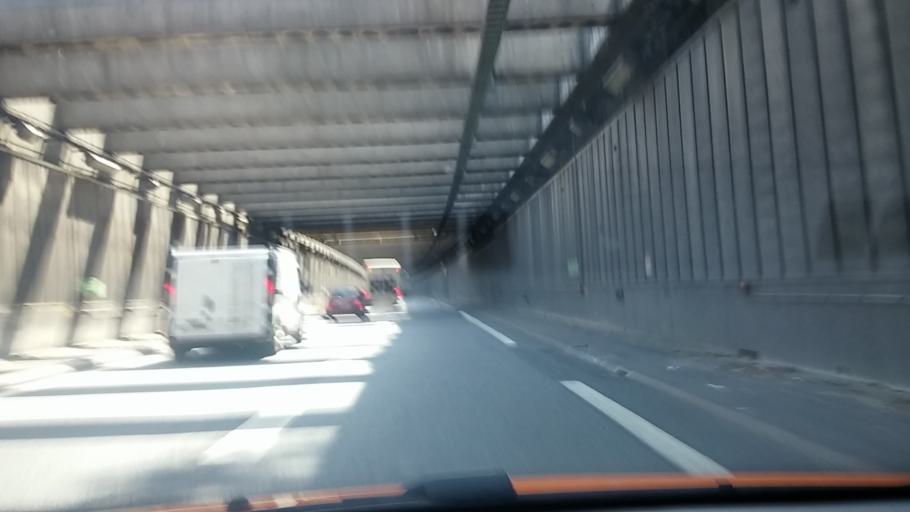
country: FR
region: Ile-de-France
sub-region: Departement du Val-de-Marne
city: Le Perreux-sur-Marne
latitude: 48.8458
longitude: 2.4917
